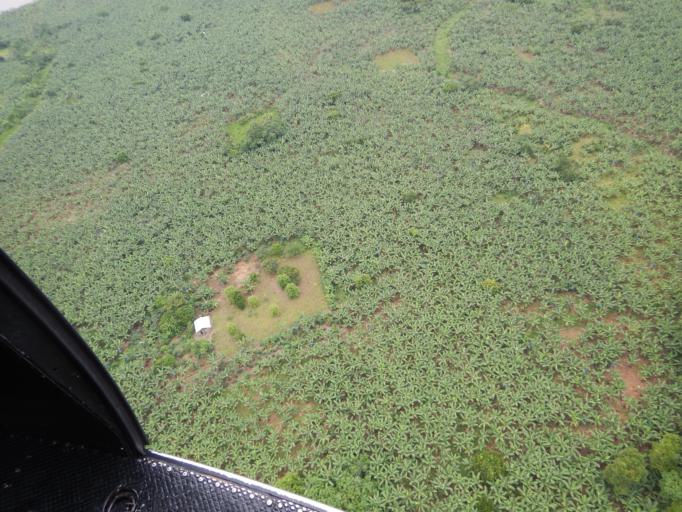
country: BO
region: Cochabamba
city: Chimore
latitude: -17.1277
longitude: -64.8240
